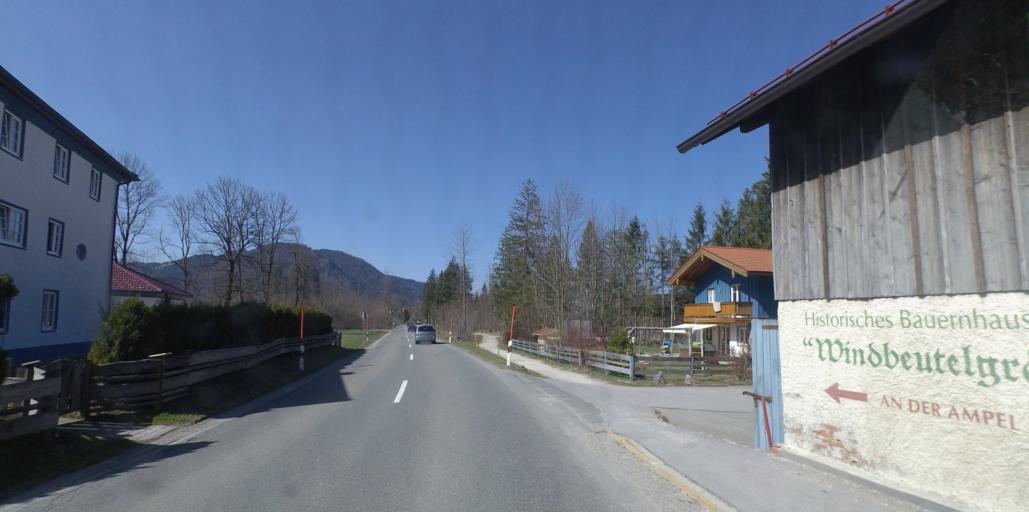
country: DE
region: Bavaria
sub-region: Upper Bavaria
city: Ruhpolding
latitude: 47.7450
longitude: 12.6572
